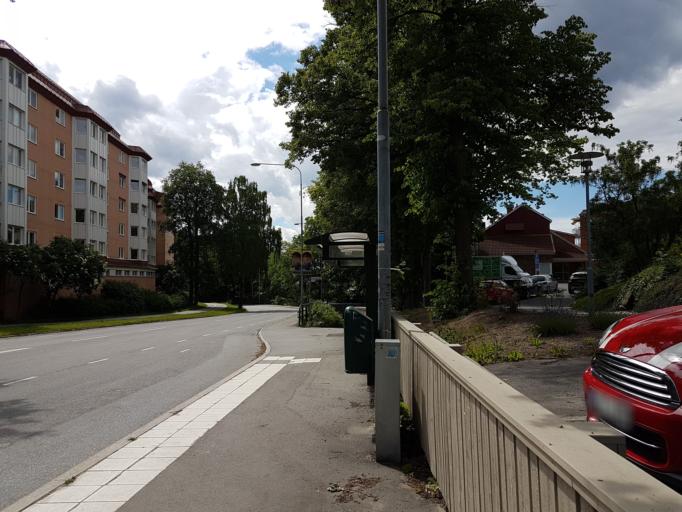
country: SE
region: Stockholm
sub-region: Lidingo
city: Lidingoe
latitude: 59.3622
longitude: 18.1215
